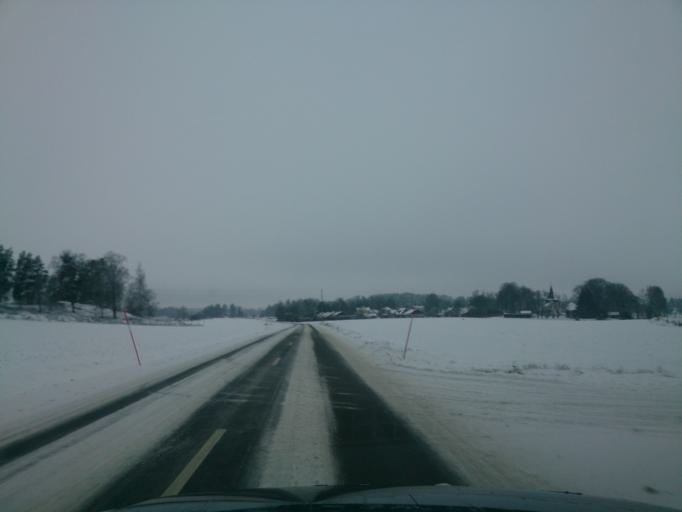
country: SE
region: OEstergoetland
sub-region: Norrkopings Kommun
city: Kimstad
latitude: 58.4089
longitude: 15.9322
